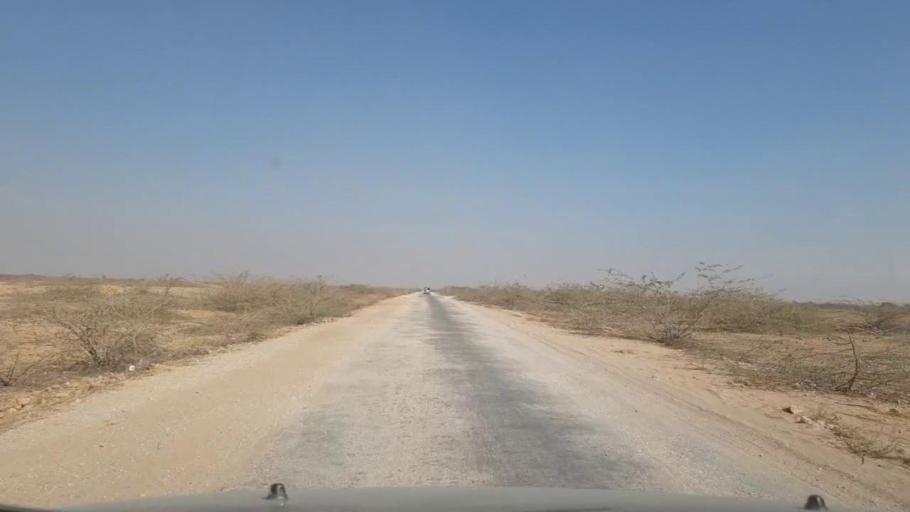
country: PK
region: Sindh
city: Thatta
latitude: 24.8925
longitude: 67.9150
